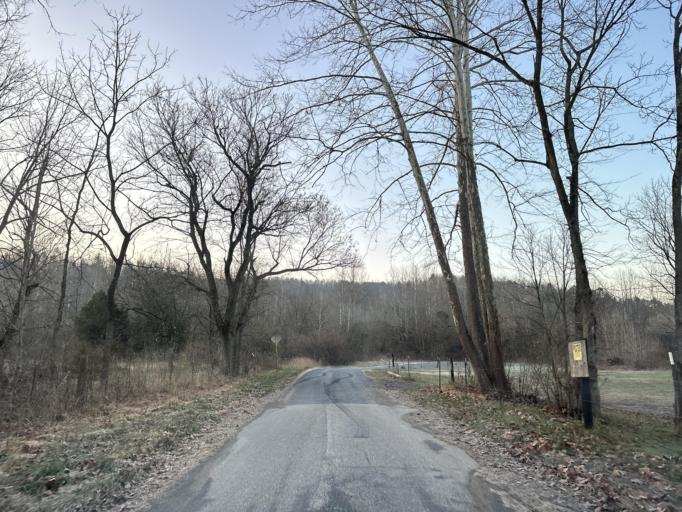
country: US
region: Virginia
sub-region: Rockbridge County
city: East Lexington
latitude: 38.0776
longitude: -79.3678
